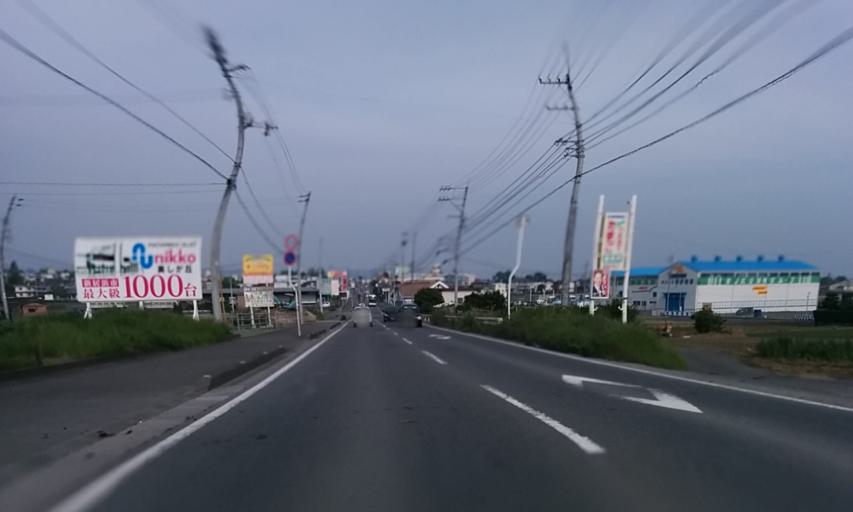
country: JP
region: Ehime
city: Kawanoecho
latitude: 33.9664
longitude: 133.4912
